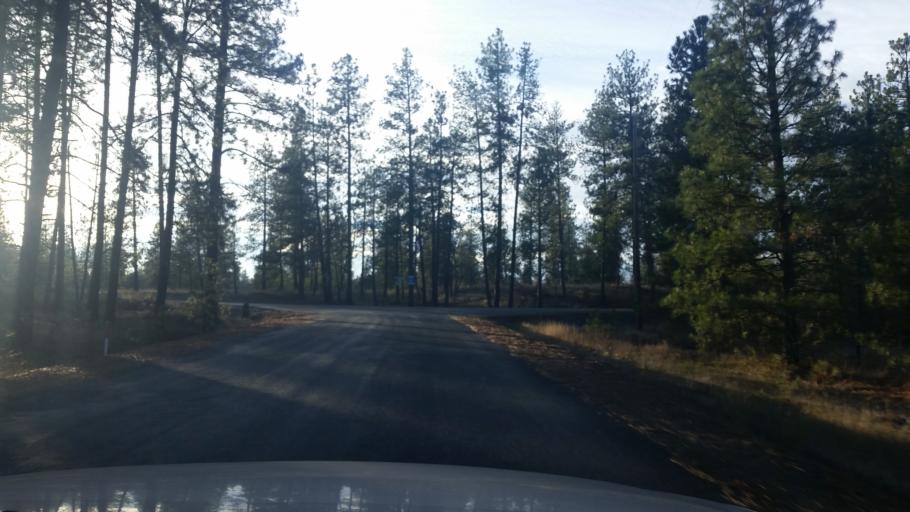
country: US
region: Washington
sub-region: Spokane County
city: Cheney
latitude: 47.5176
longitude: -117.4867
